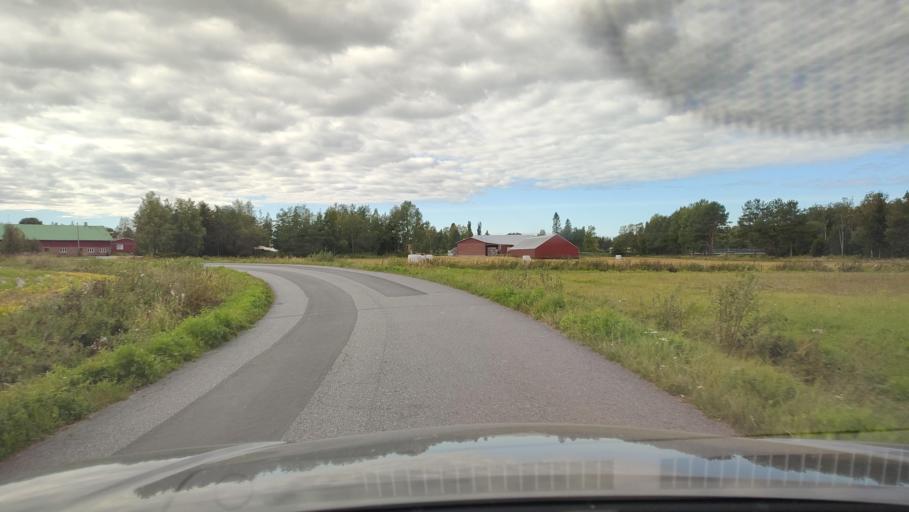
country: FI
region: Southern Ostrobothnia
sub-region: Suupohja
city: Karijoki
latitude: 62.2377
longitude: 21.5831
